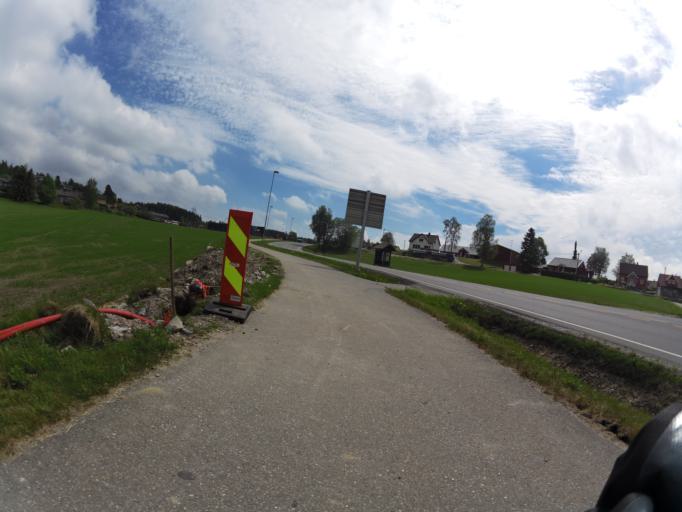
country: NO
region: Ostfold
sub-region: Rade
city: Karlshus
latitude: 59.3447
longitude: 10.9311
